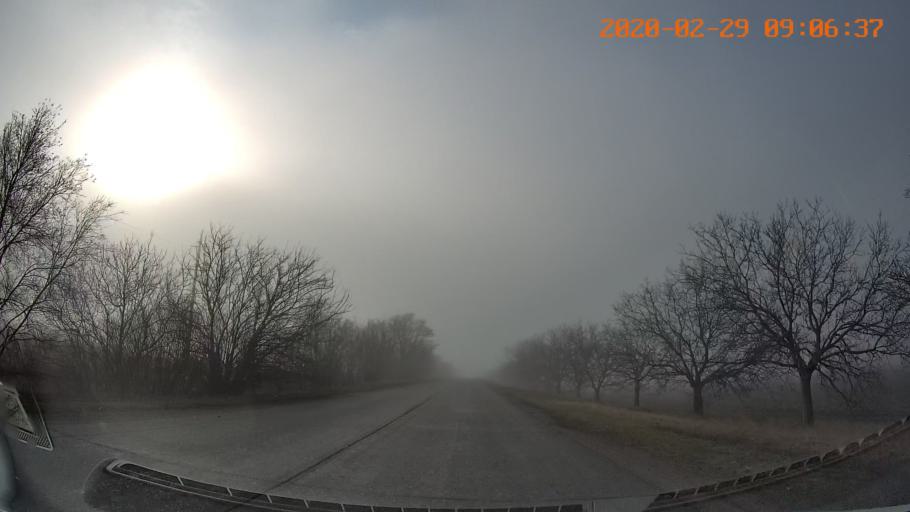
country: MD
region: Telenesti
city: Tiraspolul Nou
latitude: 46.8732
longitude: 29.7454
